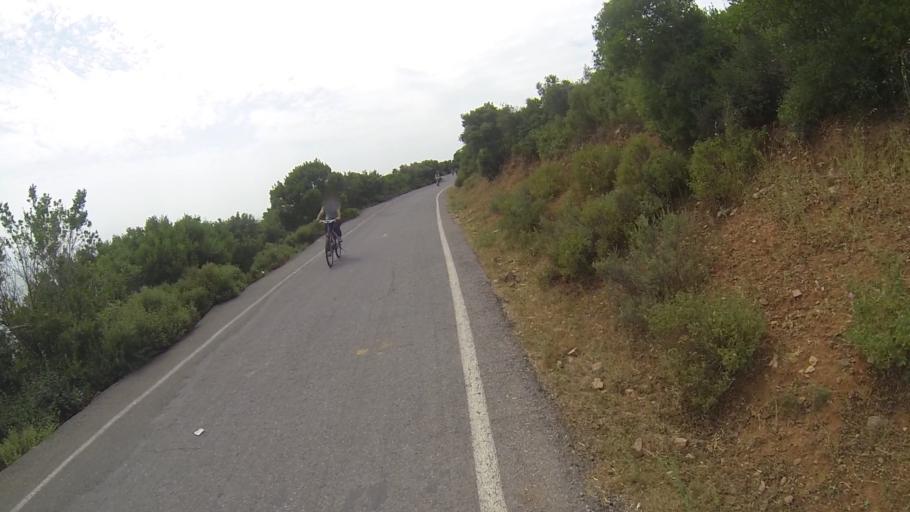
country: TR
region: Istanbul
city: Adalar
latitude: 40.8391
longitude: 29.1220
